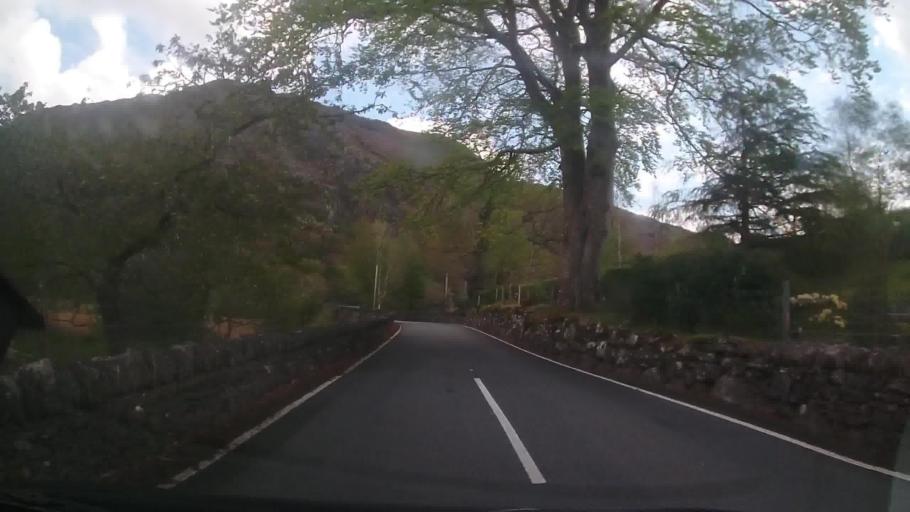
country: GB
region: Wales
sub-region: Gwynedd
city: Porthmadog
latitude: 53.0066
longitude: -4.1039
